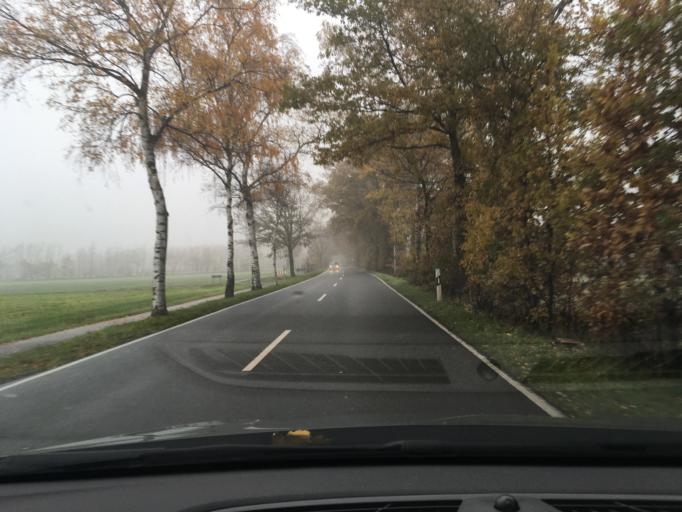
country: DE
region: North Rhine-Westphalia
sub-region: Regierungsbezirk Munster
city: Ahaus
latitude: 52.1035
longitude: 6.9155
